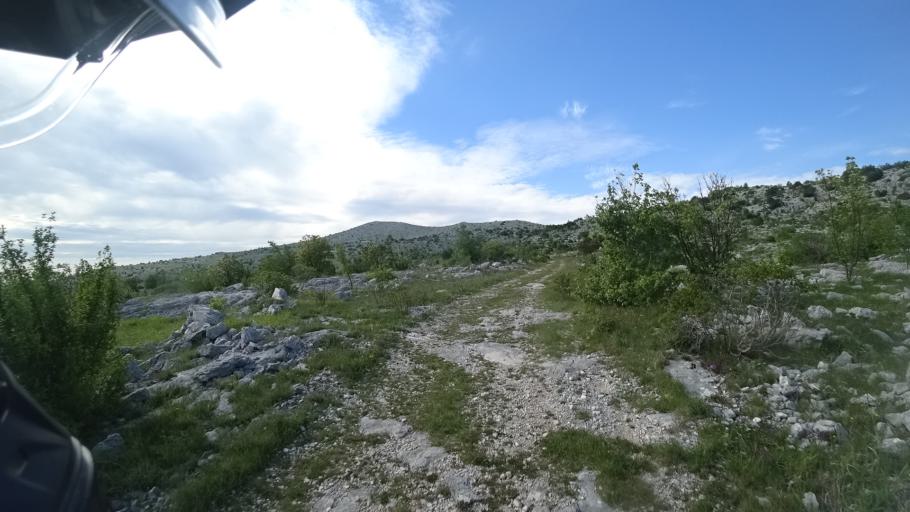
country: HR
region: Splitsko-Dalmatinska
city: Hrvace
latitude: 43.7962
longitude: 16.4335
